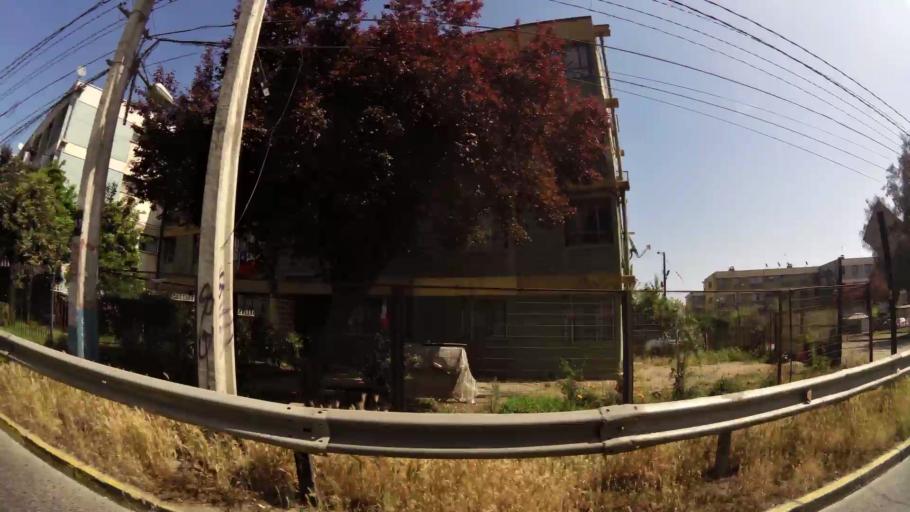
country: CL
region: Santiago Metropolitan
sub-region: Provincia de Santiago
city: Villa Presidente Frei, Nunoa, Santiago, Chile
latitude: -33.4664
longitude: -70.5502
